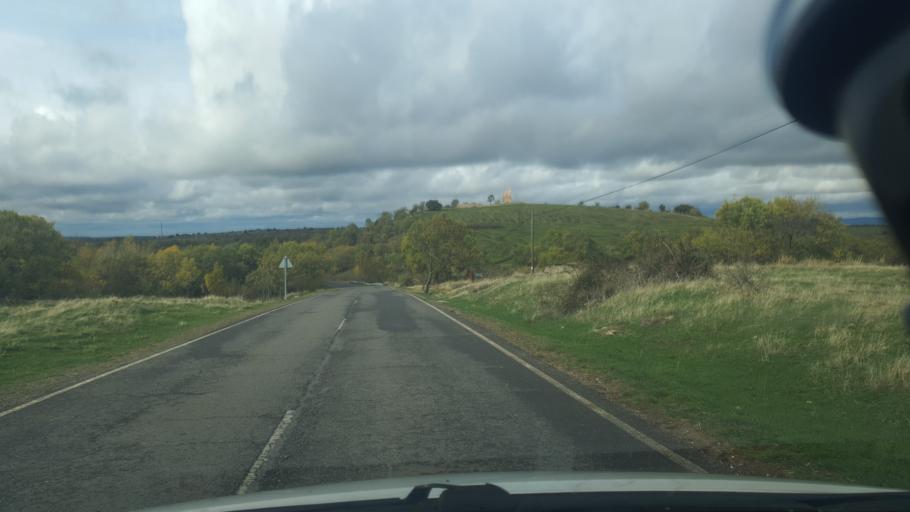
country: ES
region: Castille and Leon
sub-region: Provincia de Segovia
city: Gallegos
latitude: 41.0788
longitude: -3.7870
